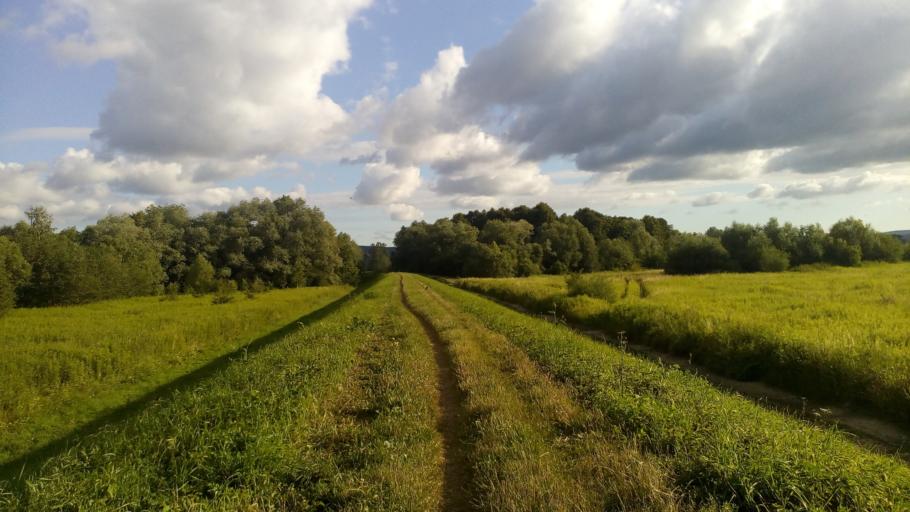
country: PL
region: Lesser Poland Voivodeship
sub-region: Powiat nowosadecki
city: Stary Sacz
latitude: 49.5863
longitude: 20.6542
